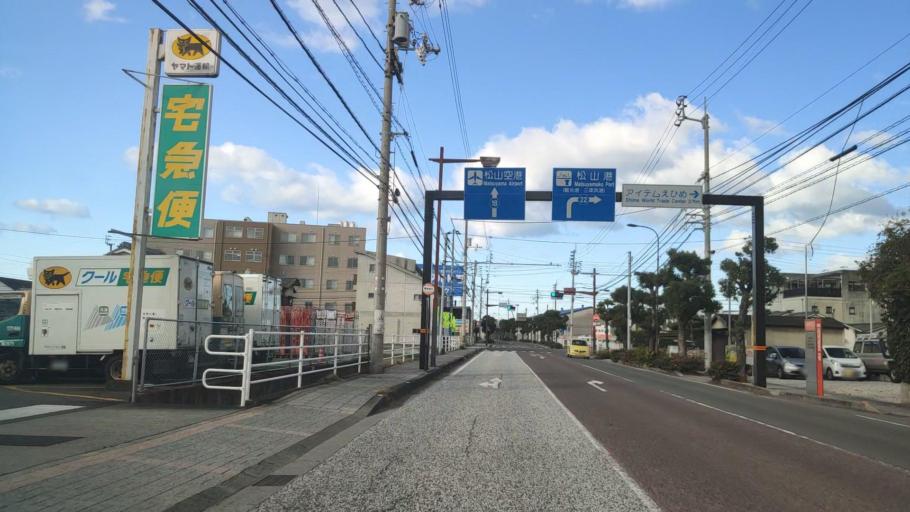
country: JP
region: Ehime
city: Masaki-cho
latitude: 33.8283
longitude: 132.7097
